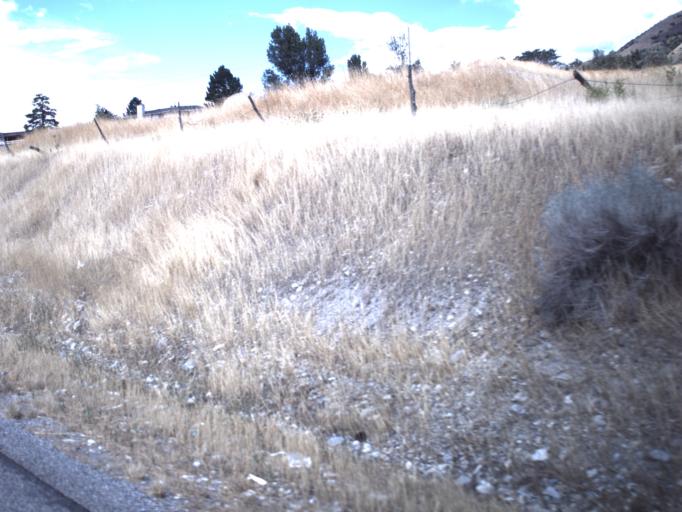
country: US
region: Utah
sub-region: Box Elder County
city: Elwood
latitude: 41.7338
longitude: -112.0986
